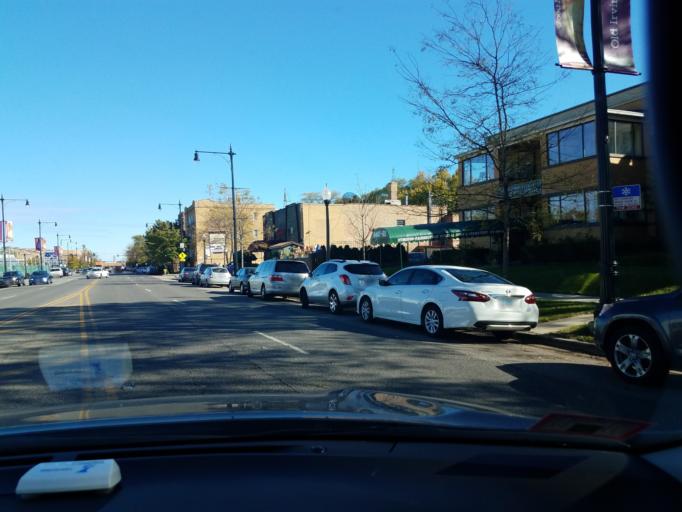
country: US
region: Illinois
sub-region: Cook County
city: Lincolnwood
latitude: 41.9535
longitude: -87.7403
